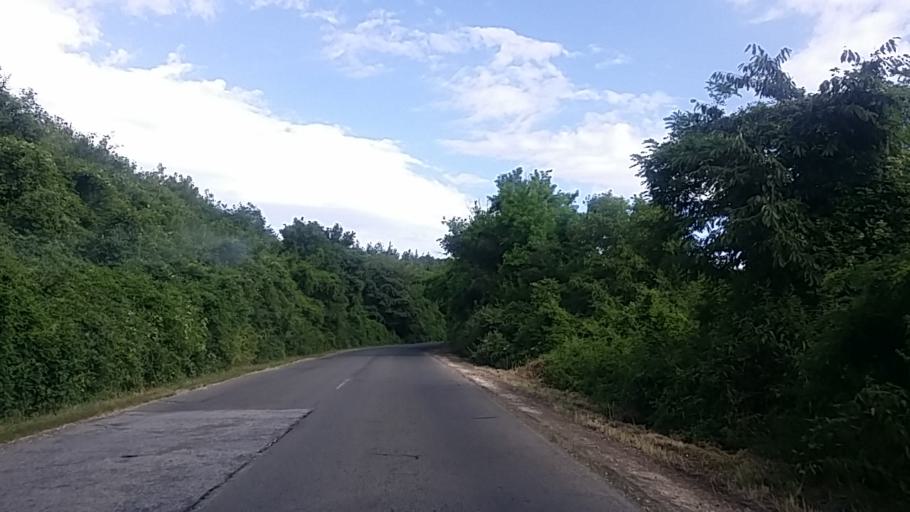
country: HU
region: Pest
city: Kosd
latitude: 47.8207
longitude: 19.2337
